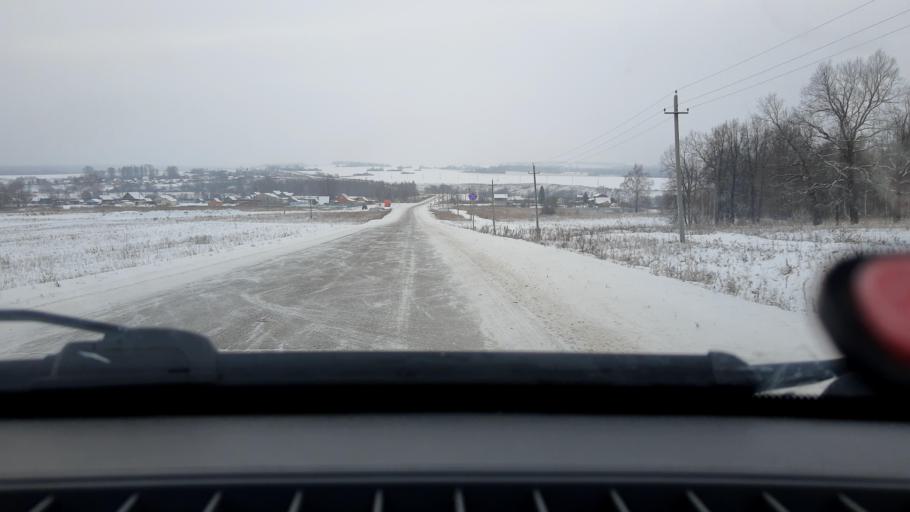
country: RU
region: Bashkortostan
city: Iglino
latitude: 54.6479
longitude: 56.4261
